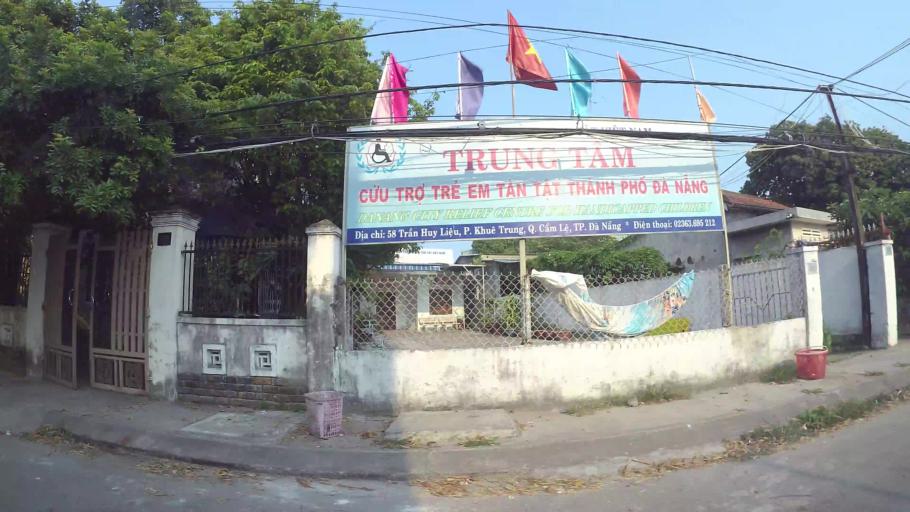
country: VN
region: Da Nang
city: Cam Le
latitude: 16.0208
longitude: 108.2049
